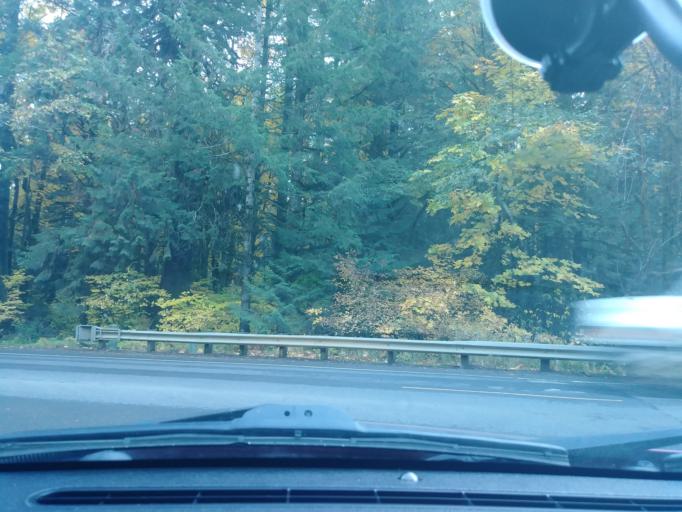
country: US
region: Oregon
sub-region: Washington County
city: Banks
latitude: 45.6542
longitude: -123.3011
